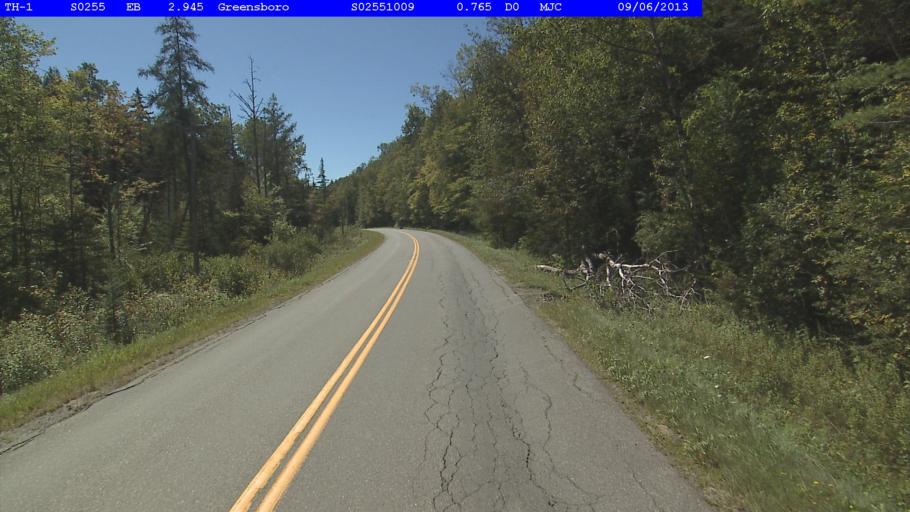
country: US
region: Vermont
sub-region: Caledonia County
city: Hardwick
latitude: 44.6299
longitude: -72.3281
